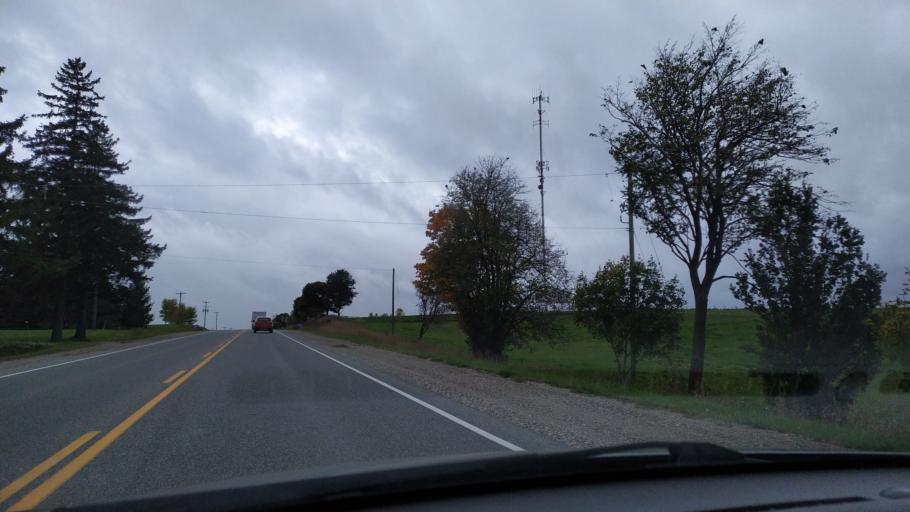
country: CA
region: Ontario
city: Stratford
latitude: 43.3694
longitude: -80.8180
